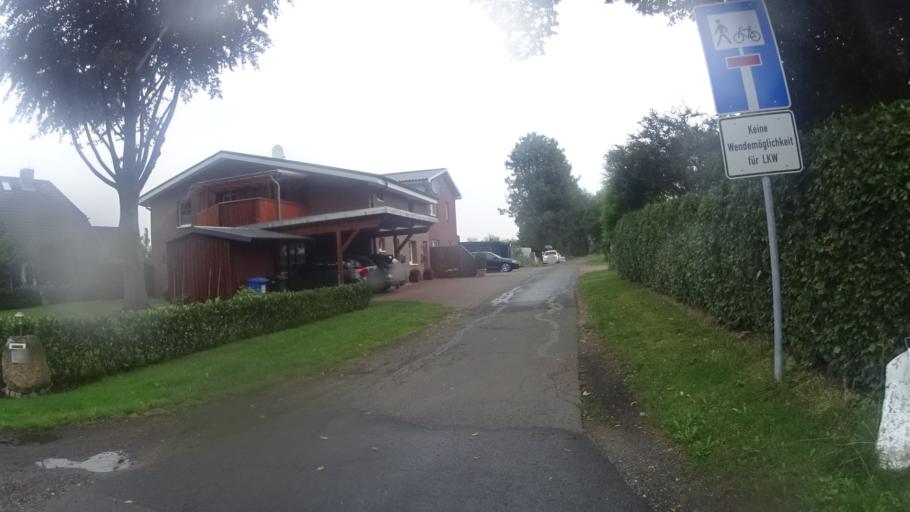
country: DE
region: Schleswig-Holstein
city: Hemdingen
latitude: 53.7643
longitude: 9.8230
